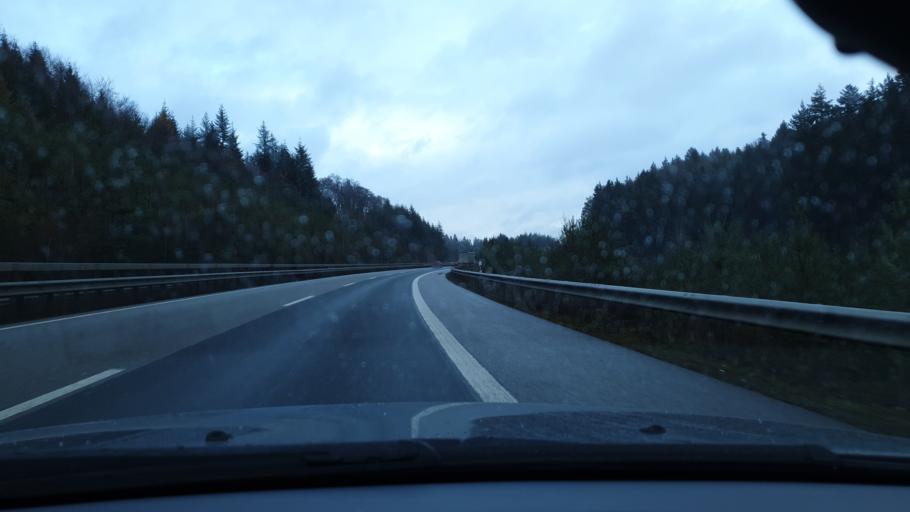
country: DE
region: Rheinland-Pfalz
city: Mehlingen
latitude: 49.4722
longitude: 7.8262
